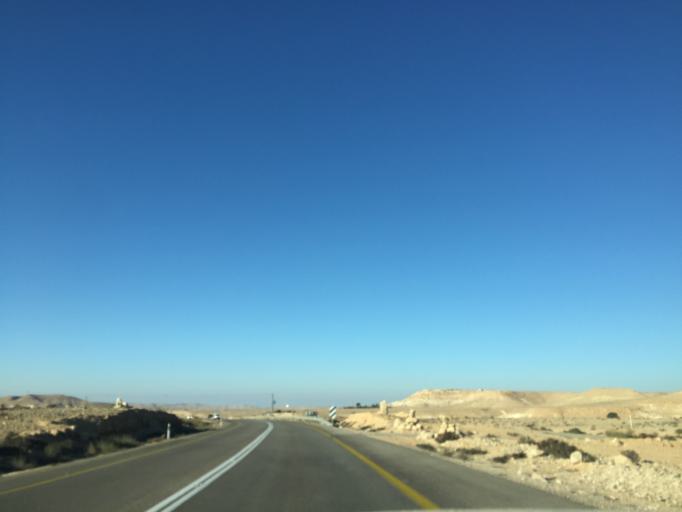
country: IL
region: Southern District
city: Midreshet Ben-Gurion
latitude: 30.7721
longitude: 34.7717
